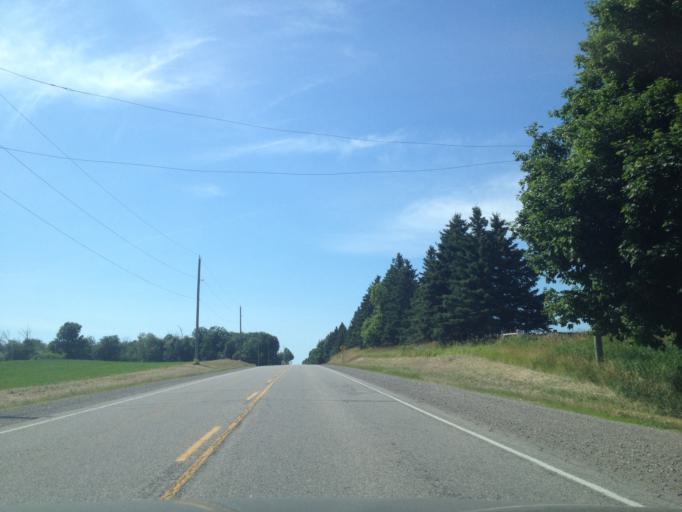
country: CA
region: Ontario
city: Stratford
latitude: 43.4719
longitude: -80.8052
